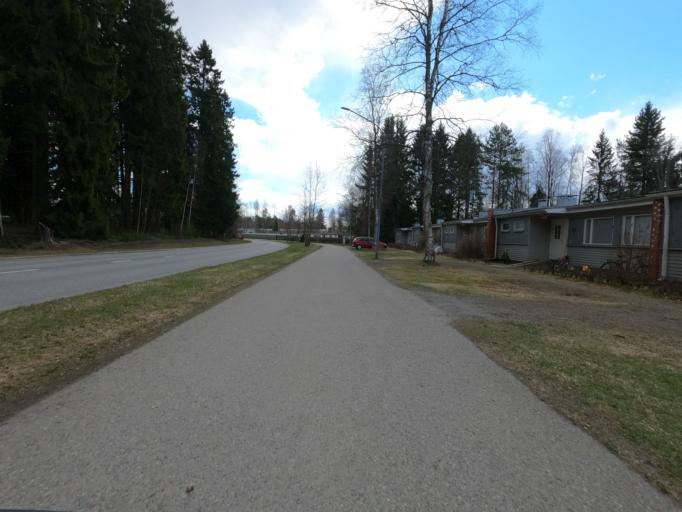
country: FI
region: North Karelia
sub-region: Joensuu
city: Joensuu
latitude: 62.5843
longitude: 29.7783
